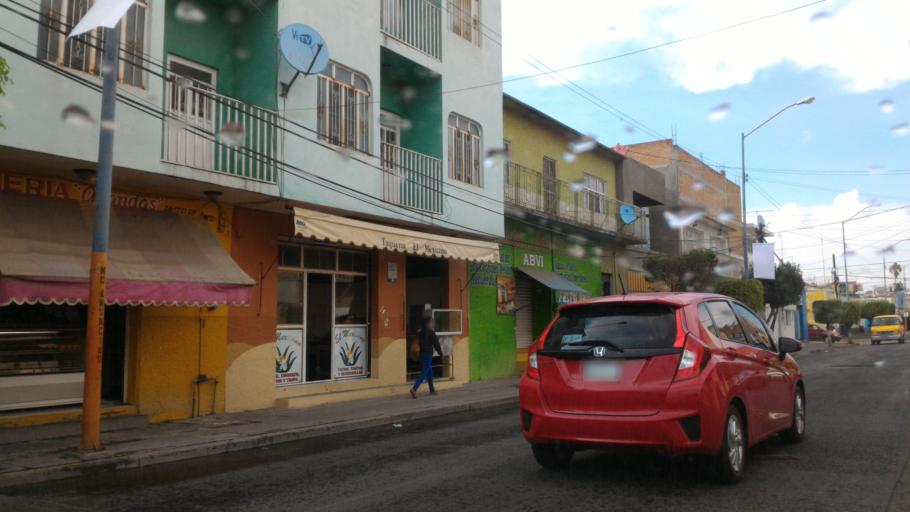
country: MX
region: Guanajuato
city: Ciudad Manuel Doblado
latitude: 20.7289
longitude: -101.9512
